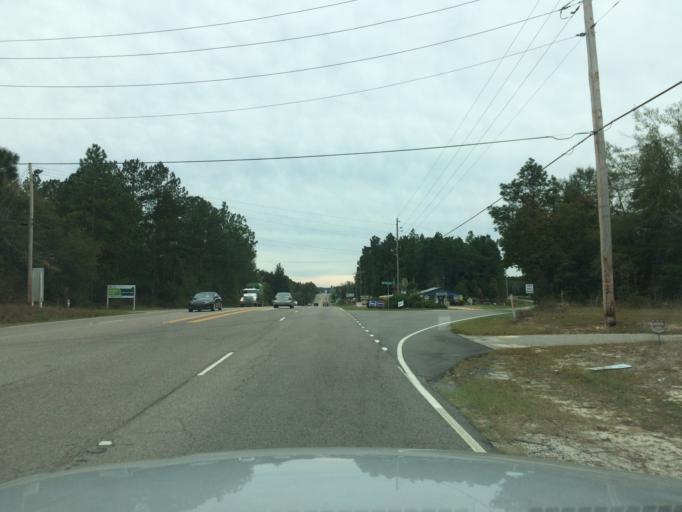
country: US
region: South Carolina
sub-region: Aiken County
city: New Ellenton
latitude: 33.4355
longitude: -81.6862
